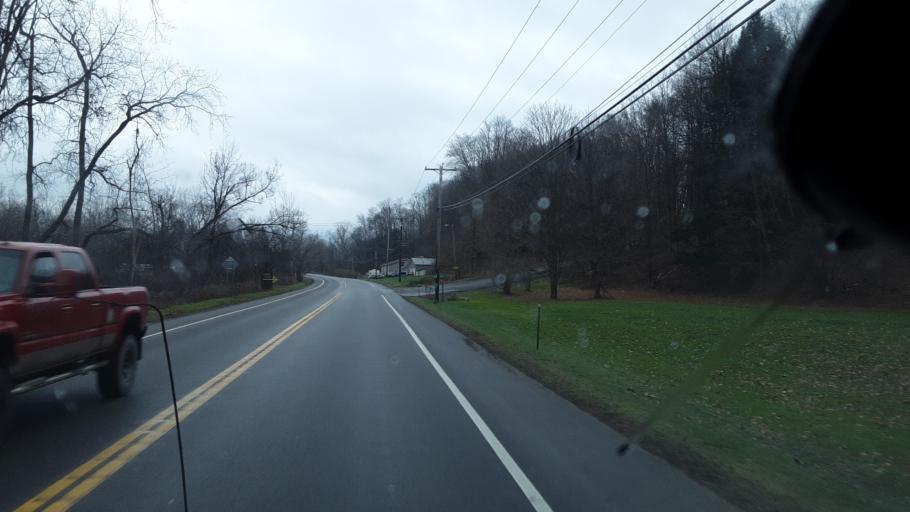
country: US
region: New York
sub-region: Wyoming County
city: Arcade
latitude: 42.4885
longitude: -78.3728
